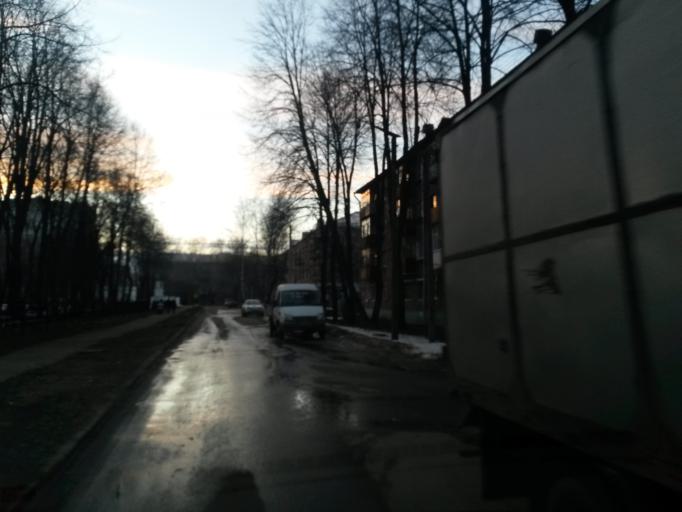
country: RU
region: Jaroslavl
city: Yaroslavl
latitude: 57.6335
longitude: 39.8387
